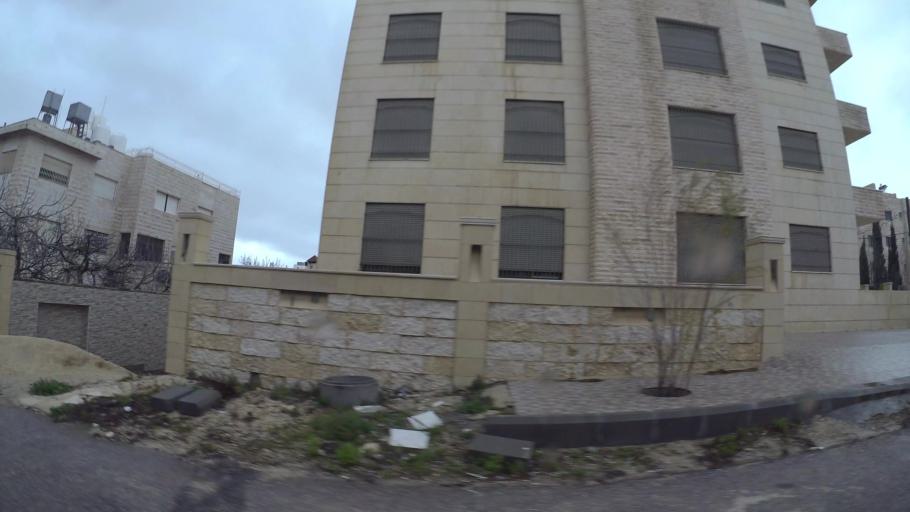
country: JO
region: Amman
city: Al Jubayhah
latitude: 32.0355
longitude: 35.8604
